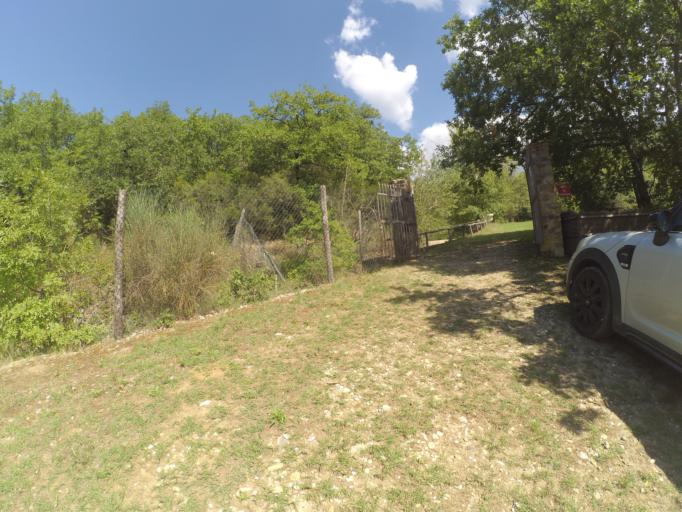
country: IT
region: Tuscany
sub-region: Province of Arezzo
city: Castiglion Fibocchi
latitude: 43.5421
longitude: 11.7699
